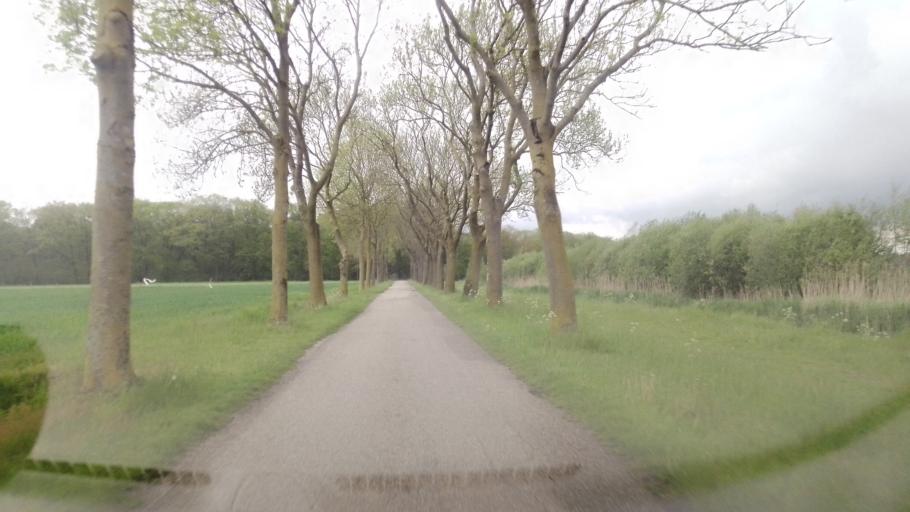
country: NL
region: Limburg
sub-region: Gemeente Venlo
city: Arcen
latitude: 51.4687
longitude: 6.2159
